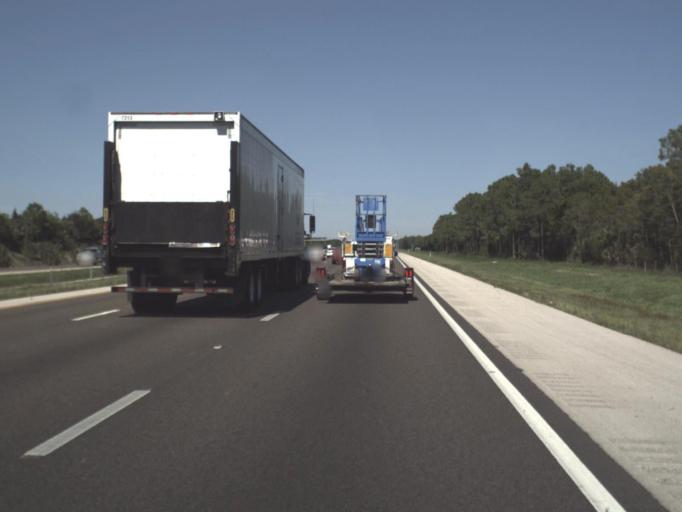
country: US
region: Florida
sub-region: Lee County
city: Bonita Springs
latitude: 26.2906
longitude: -81.7427
